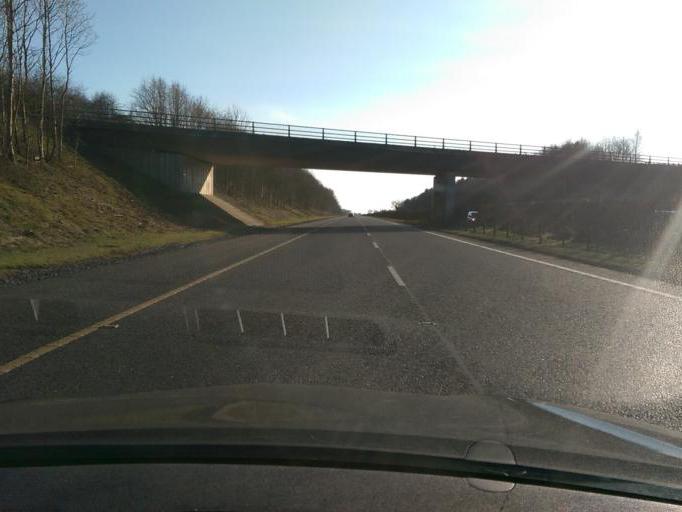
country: IE
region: Leinster
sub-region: Laois
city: Portlaoise
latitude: 53.0308
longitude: -7.2503
